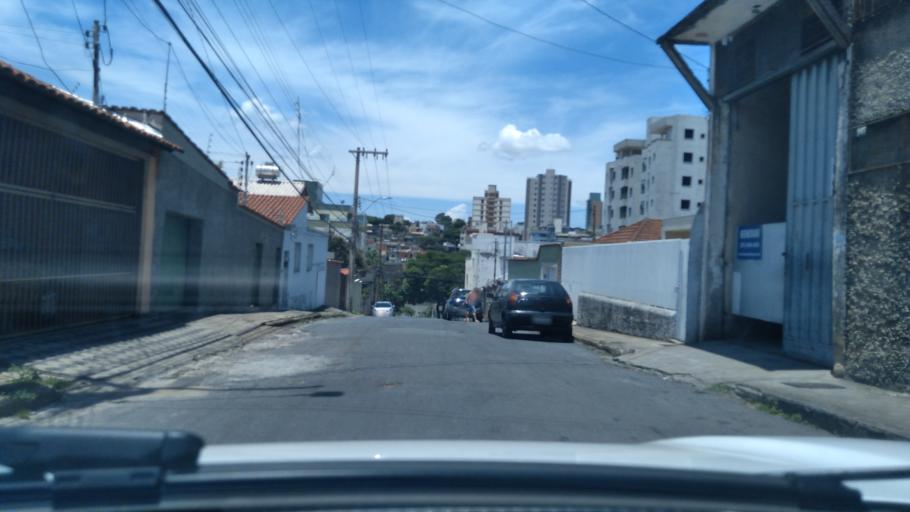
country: BR
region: Minas Gerais
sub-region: Contagem
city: Contagem
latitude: -19.9296
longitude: -43.9967
